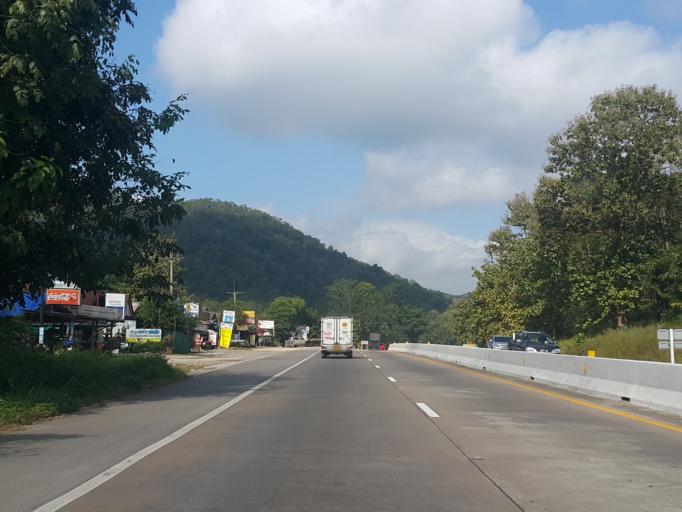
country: TH
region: Lampang
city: Hang Chat
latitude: 18.3352
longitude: 99.2493
